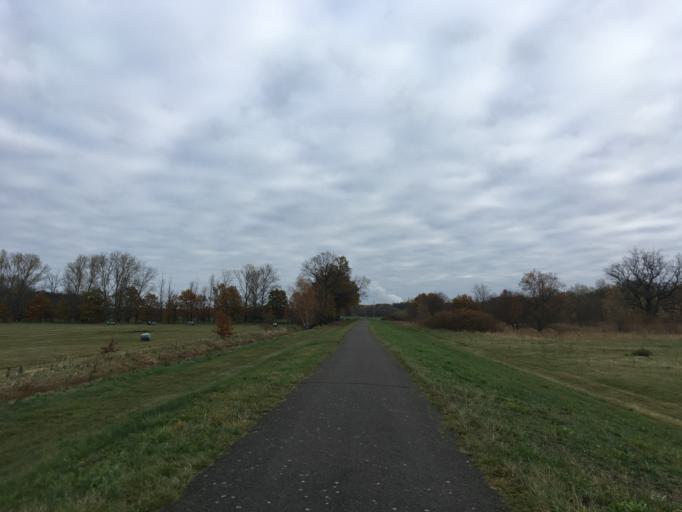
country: DE
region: Brandenburg
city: Briesen
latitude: 51.8457
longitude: 14.2797
